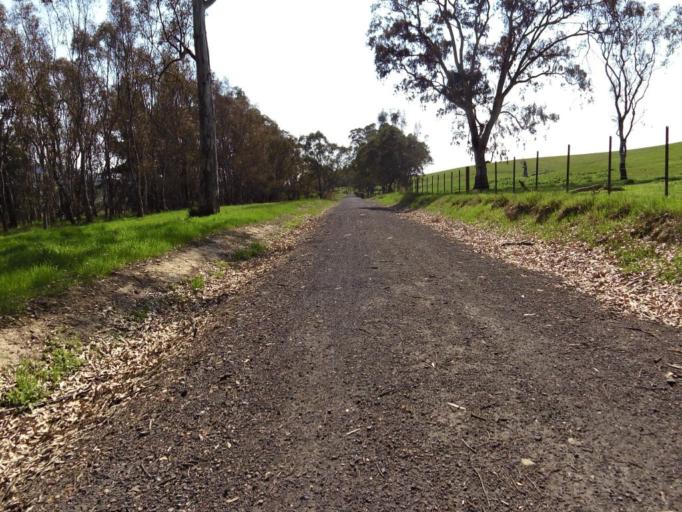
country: AU
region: Victoria
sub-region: Murrindindi
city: Alexandra
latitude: -37.1345
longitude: 145.5924
